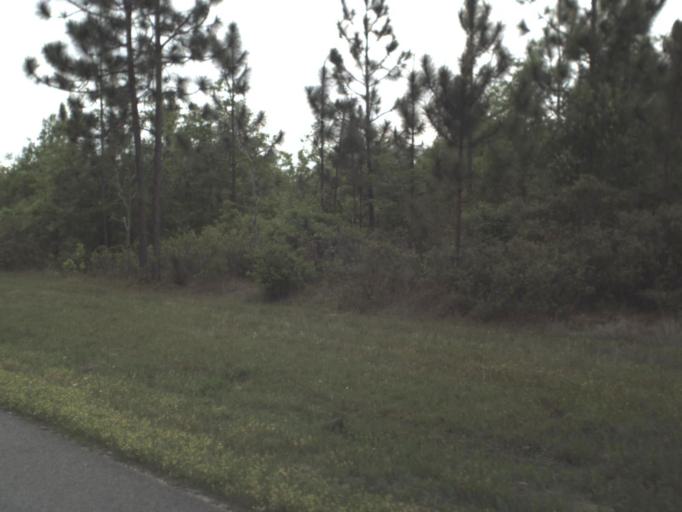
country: US
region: Alabama
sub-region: Escambia County
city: East Brewton
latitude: 30.9236
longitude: -87.0230
